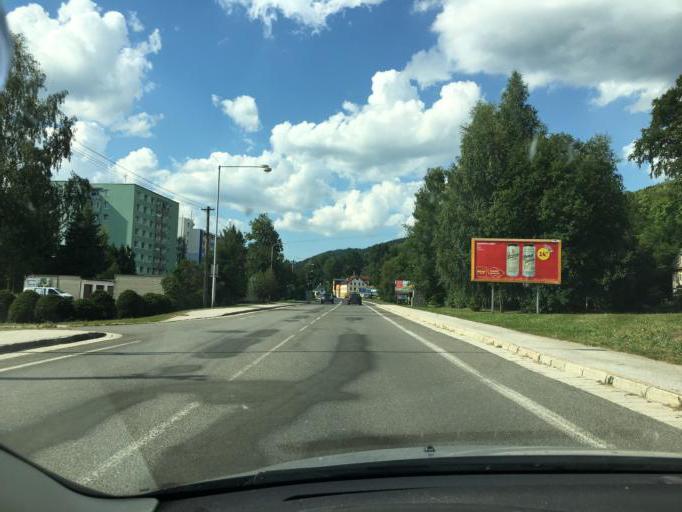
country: CZ
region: Kralovehradecky
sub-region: Okres Trutnov
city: Vrchlabi
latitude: 50.6433
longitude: 15.6089
